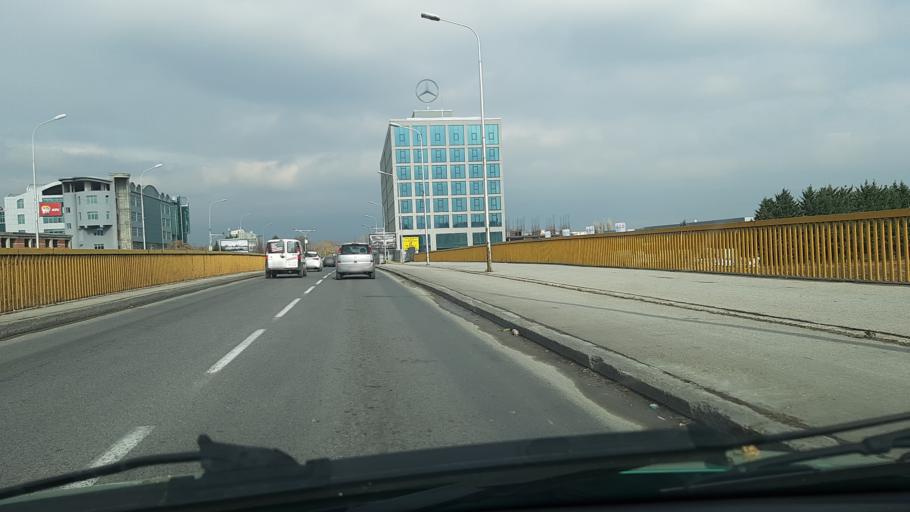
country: MK
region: Kisela Voda
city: Usje
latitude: 41.9905
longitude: 21.4744
